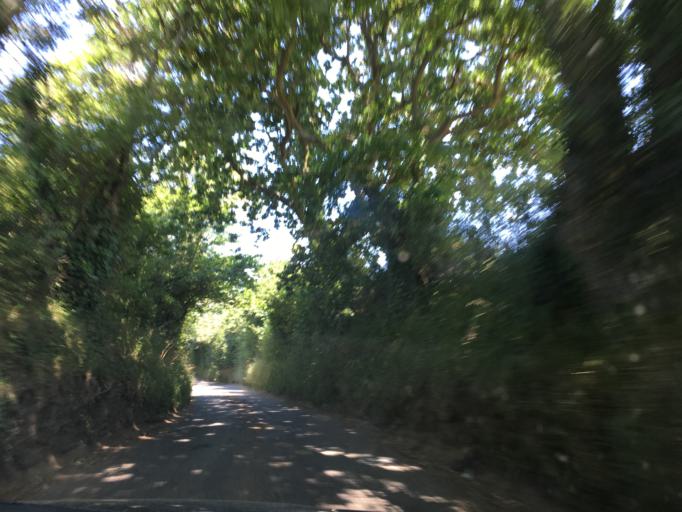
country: GB
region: England
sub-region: Isle of Wight
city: Newchurch
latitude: 50.6749
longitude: -1.2113
